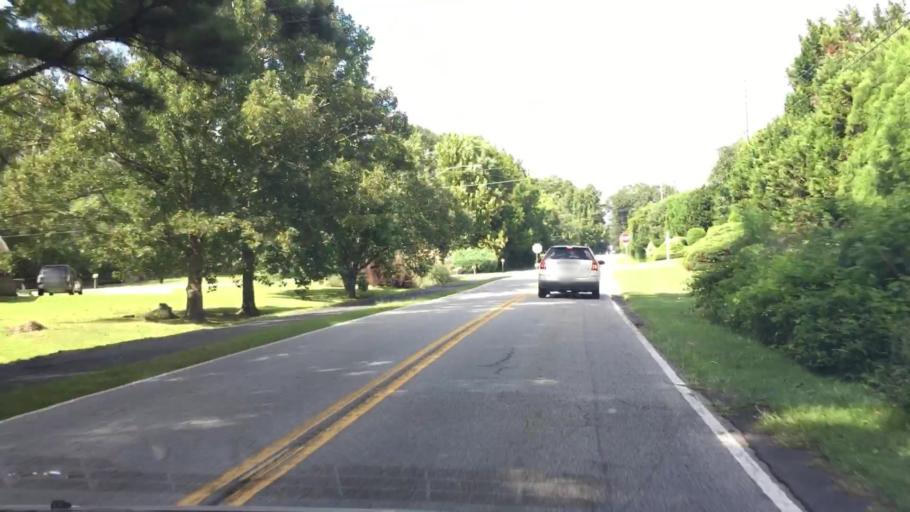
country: US
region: Georgia
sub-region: Fayette County
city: Fayetteville
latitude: 33.4372
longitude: -84.4596
